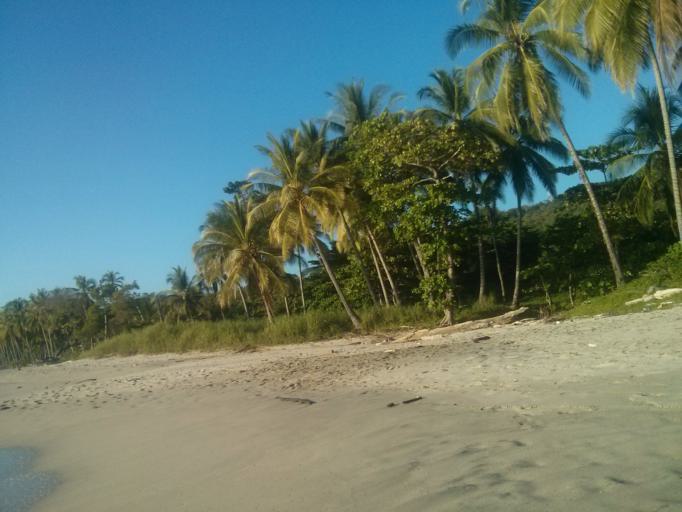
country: CR
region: Guanacaste
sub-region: Canton de Nandayure
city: Bejuco
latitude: 9.6241
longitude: -85.1498
